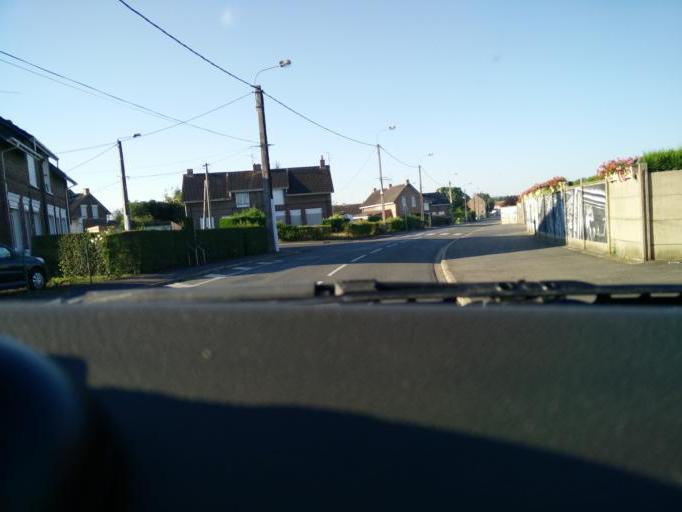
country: FR
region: Nord-Pas-de-Calais
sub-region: Departement du Pas-de-Calais
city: Grenay
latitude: 50.4553
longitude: 2.7444
